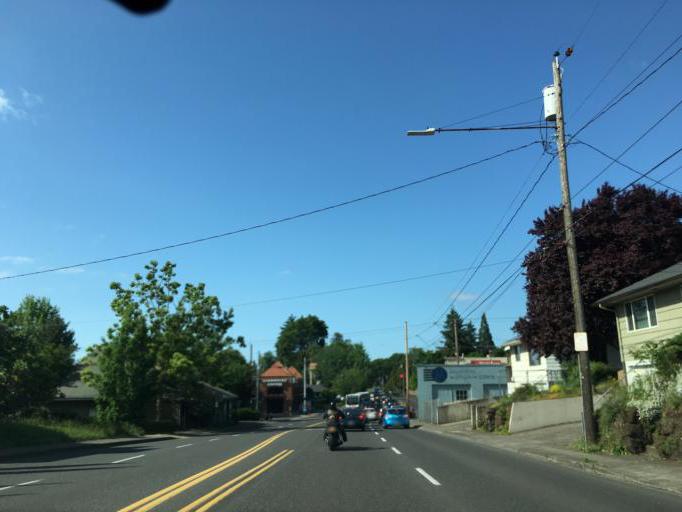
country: US
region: Oregon
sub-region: Clackamas County
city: Milwaukie
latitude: 45.4894
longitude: -122.6228
